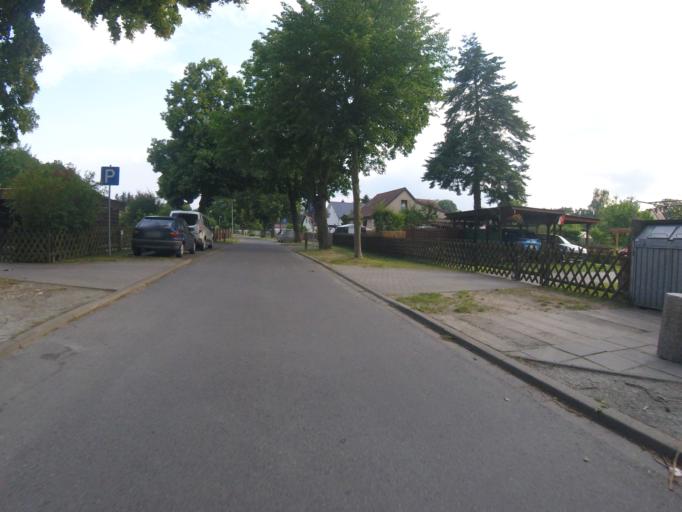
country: DE
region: Brandenburg
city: Konigs Wusterhausen
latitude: 52.2960
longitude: 13.6381
